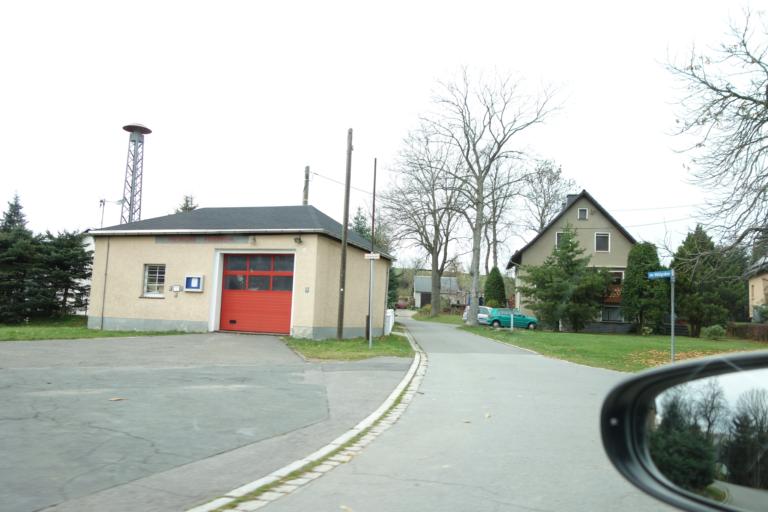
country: DE
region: Saxony
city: Eppendorf
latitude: 50.8161
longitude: 13.2568
